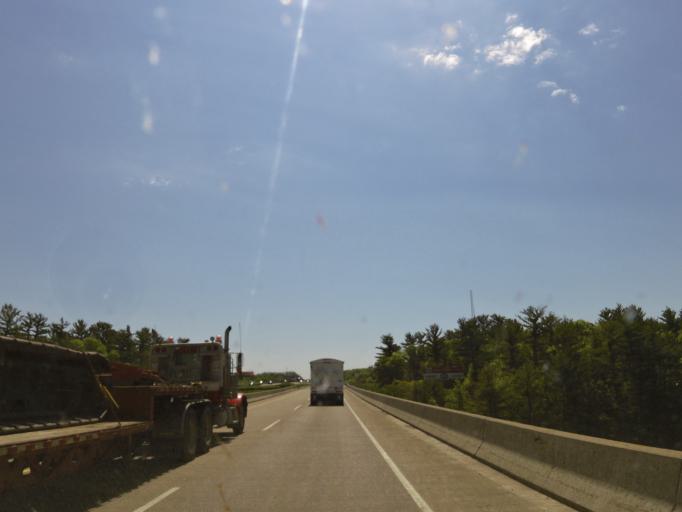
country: US
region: Wisconsin
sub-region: Jackson County
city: Black River Falls
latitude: 44.3046
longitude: -90.8342
